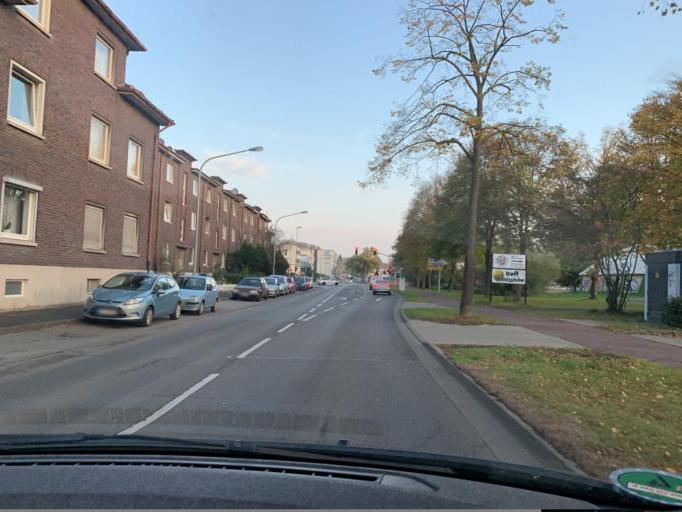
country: DE
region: North Rhine-Westphalia
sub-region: Regierungsbezirk Dusseldorf
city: Monchengladbach
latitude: 51.1459
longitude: 6.4501
